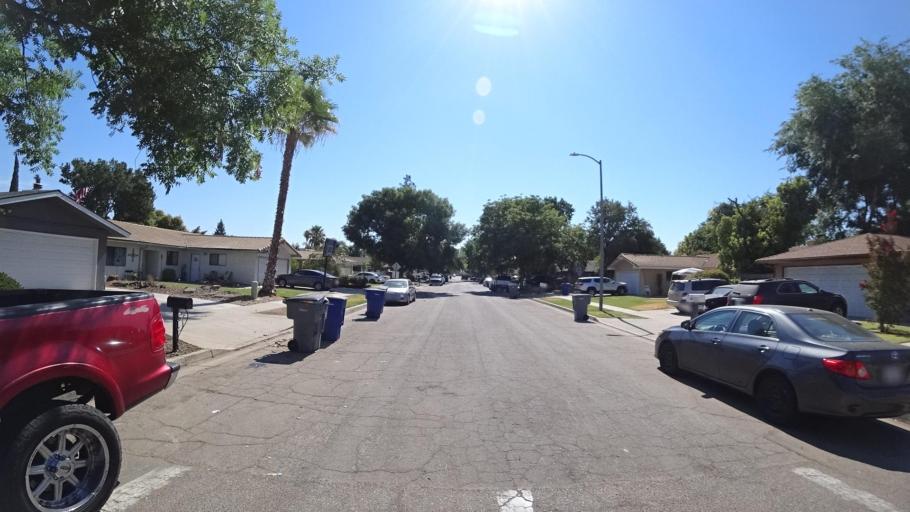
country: US
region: California
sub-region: Fresno County
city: Sunnyside
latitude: 36.7473
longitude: -119.6851
